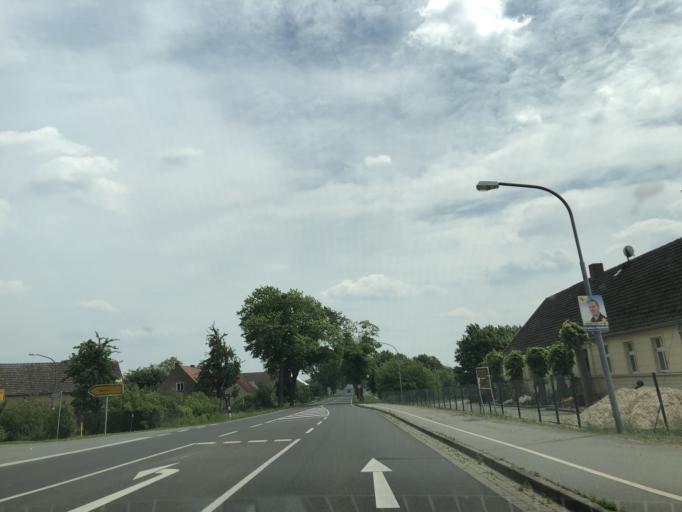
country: DE
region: Brandenburg
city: Kyritz
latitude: 52.9620
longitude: 12.3386
